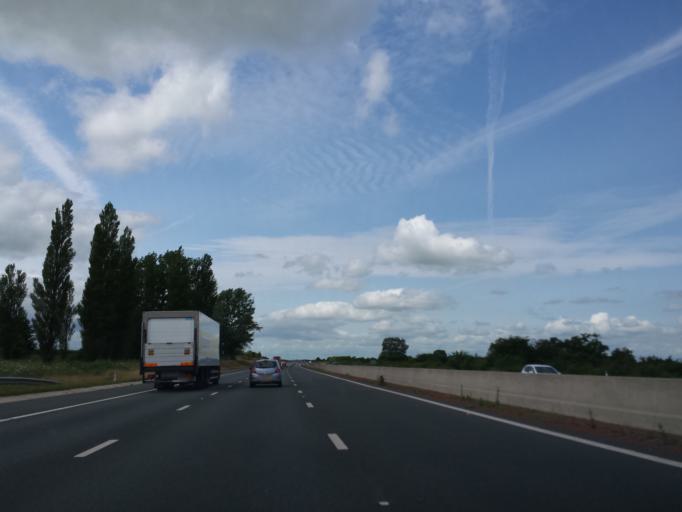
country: GB
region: England
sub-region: North Yorkshire
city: Bedale
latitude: 54.2485
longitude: -1.5056
